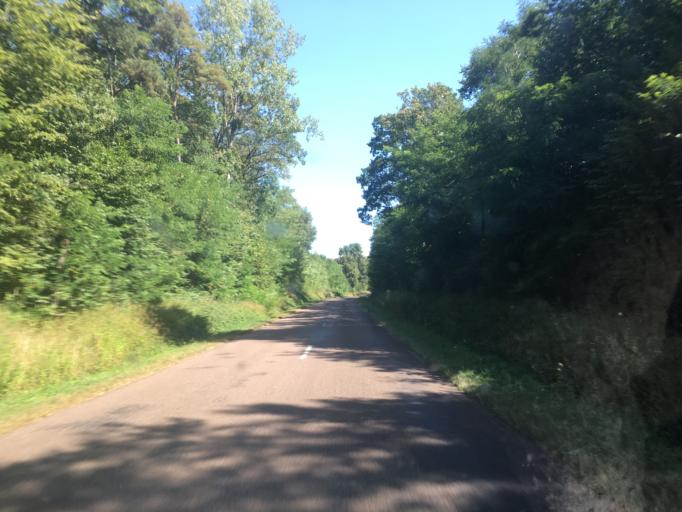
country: FR
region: Bourgogne
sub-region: Departement de l'Yonne
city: Fleury-la-Vallee
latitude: 47.8531
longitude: 3.4700
